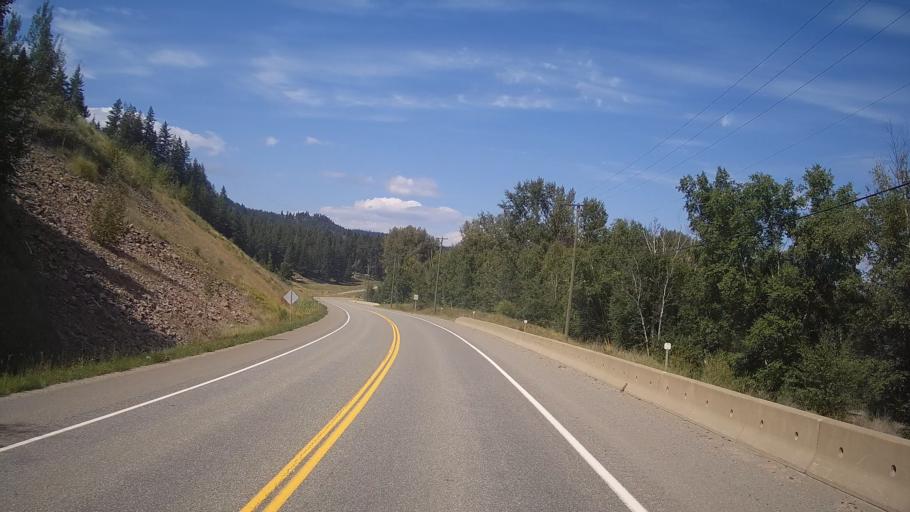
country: CA
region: British Columbia
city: Kamloops
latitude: 51.2568
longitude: -120.1767
